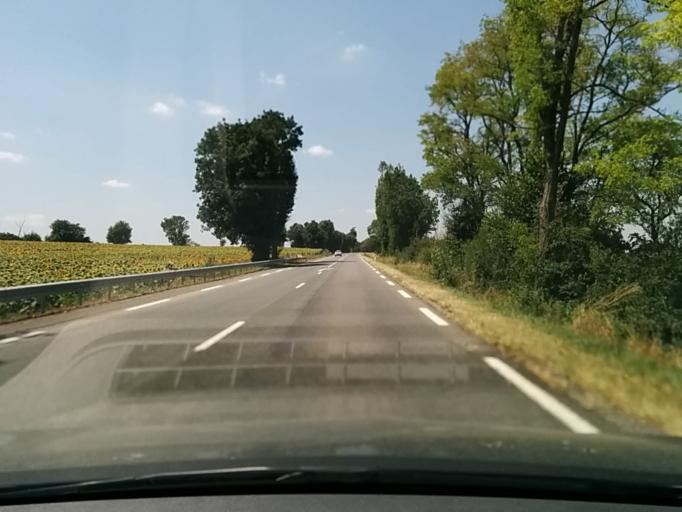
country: FR
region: Midi-Pyrenees
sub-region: Departement du Gers
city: Pujaudran
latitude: 43.6025
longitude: 1.0142
